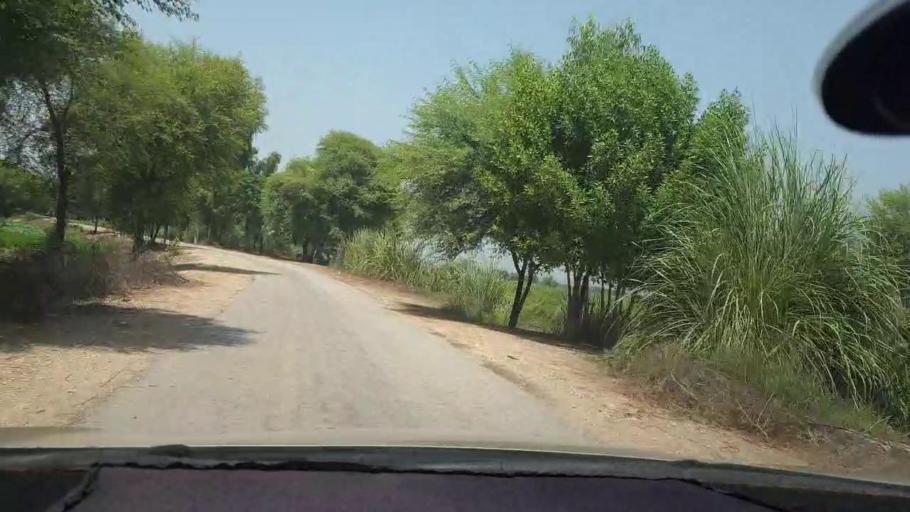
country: PK
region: Sindh
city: Kambar
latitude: 27.6623
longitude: 67.9476
